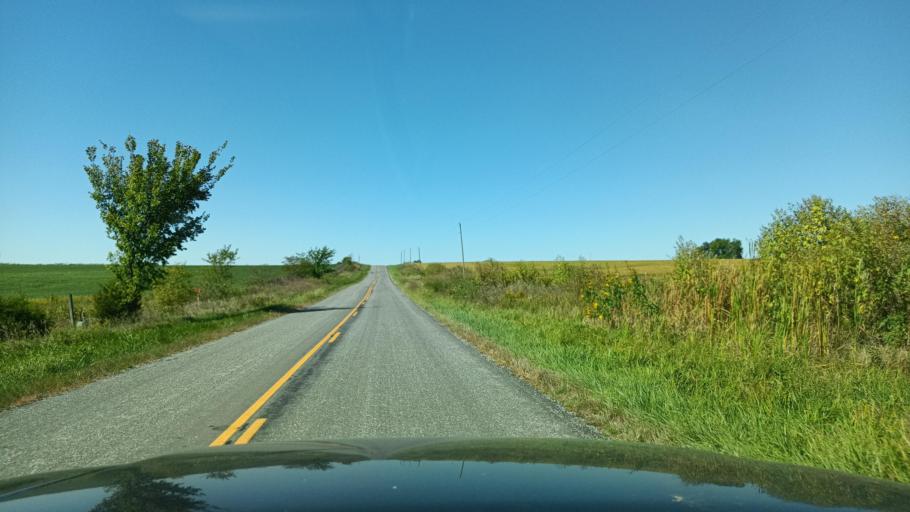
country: US
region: Missouri
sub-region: Adair County
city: Kirksville
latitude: 40.3303
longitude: -92.5262
